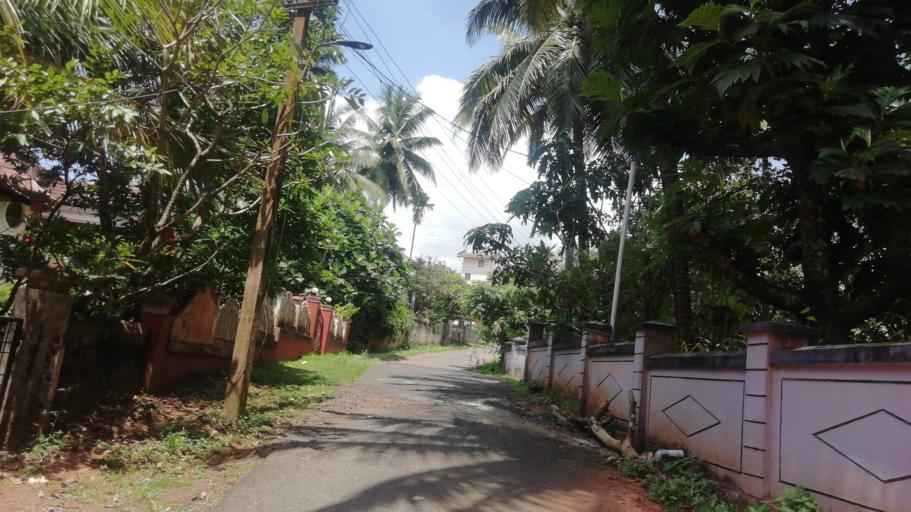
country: IN
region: Goa
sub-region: North Goa
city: Queula
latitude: 15.3854
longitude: 74.0023
